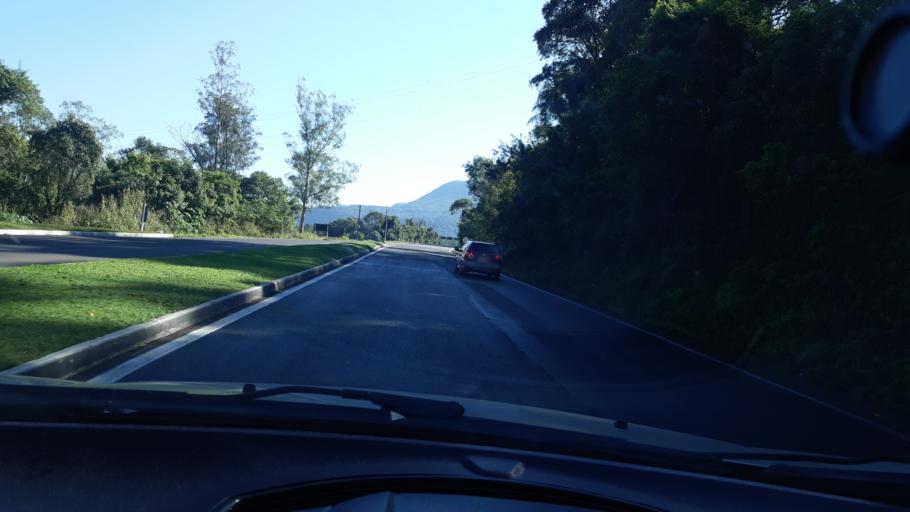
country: BR
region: Rio Grande do Sul
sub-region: Farroupilha
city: Farroupilha
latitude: -29.3733
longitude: -51.3686
